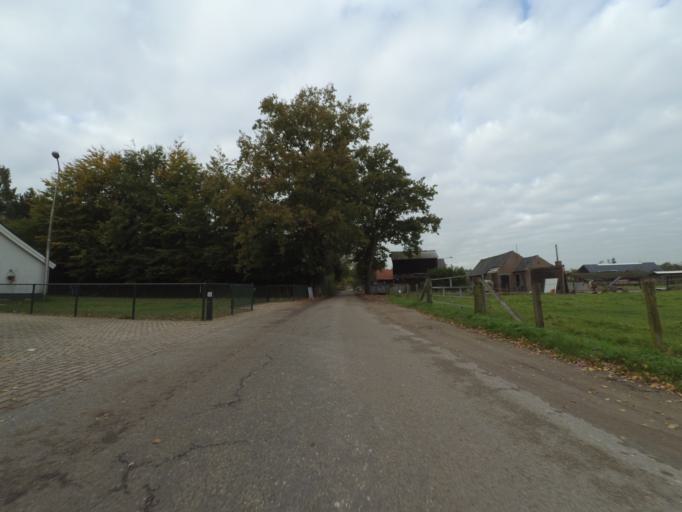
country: NL
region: Gelderland
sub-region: Gemeente Nijkerk
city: Nijkerk
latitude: 52.1952
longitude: 5.4459
